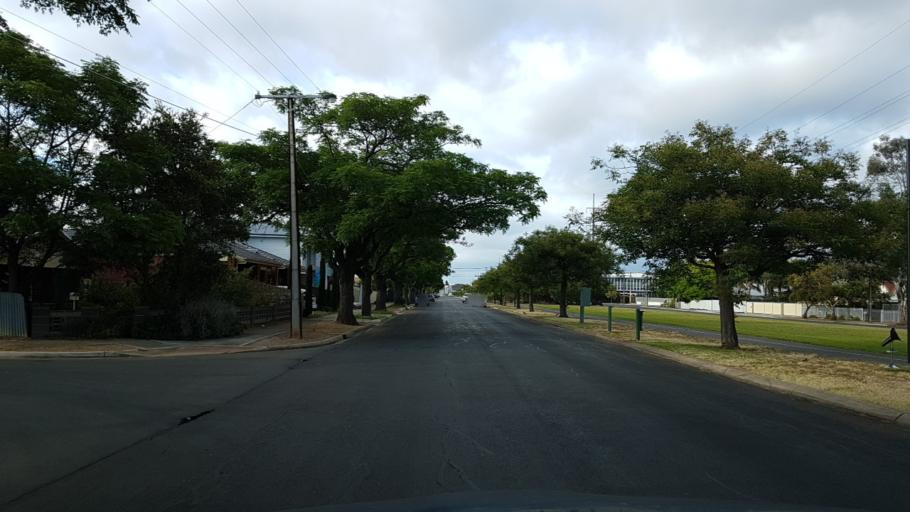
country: AU
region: South Australia
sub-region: Unley
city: Forestville
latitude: -34.9432
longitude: 138.5672
